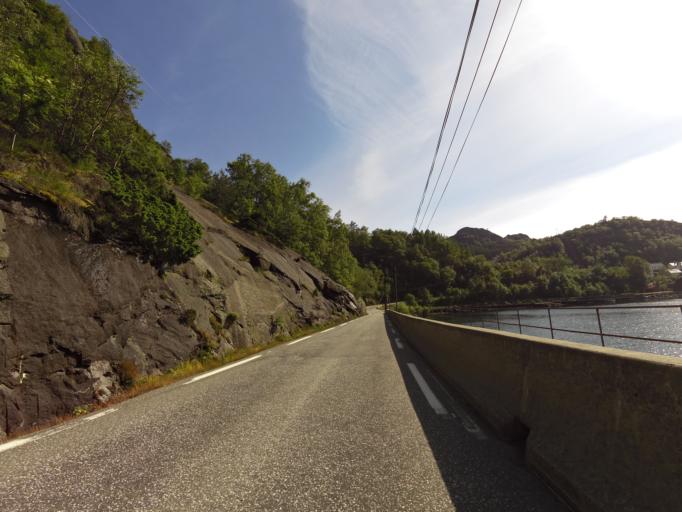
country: NO
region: Rogaland
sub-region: Sokndal
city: Hauge i Dalane
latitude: 58.3189
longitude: 6.3484
